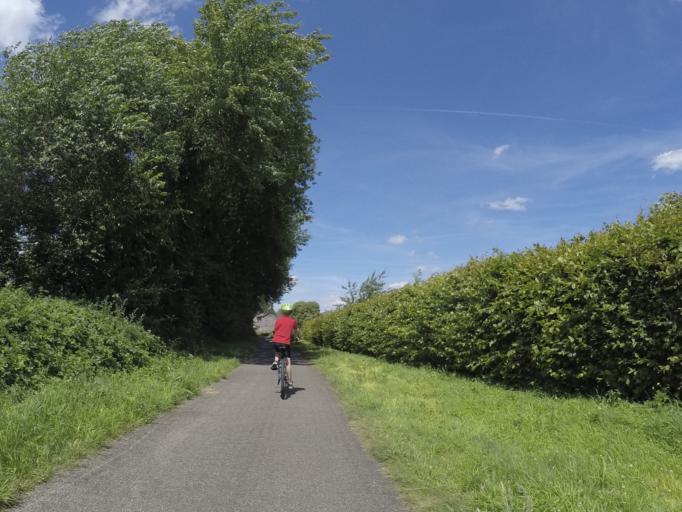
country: BE
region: Wallonia
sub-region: Province de Liege
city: Modave
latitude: 50.4269
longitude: 5.3218
